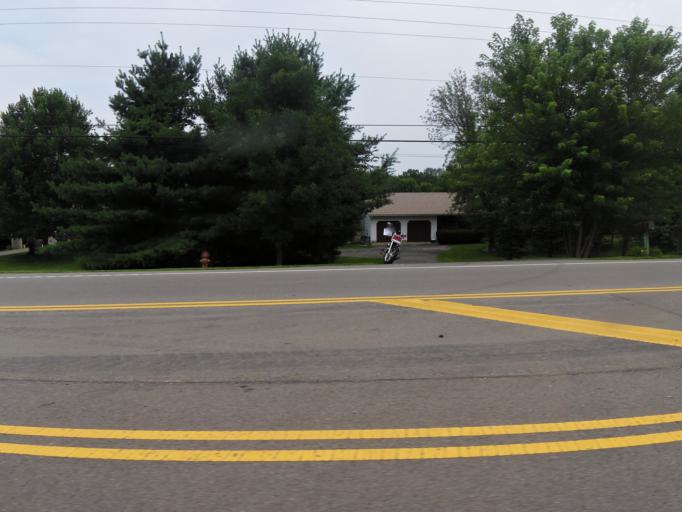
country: US
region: Ohio
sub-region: Warren County
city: Waynesville
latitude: 39.5142
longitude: -84.0356
